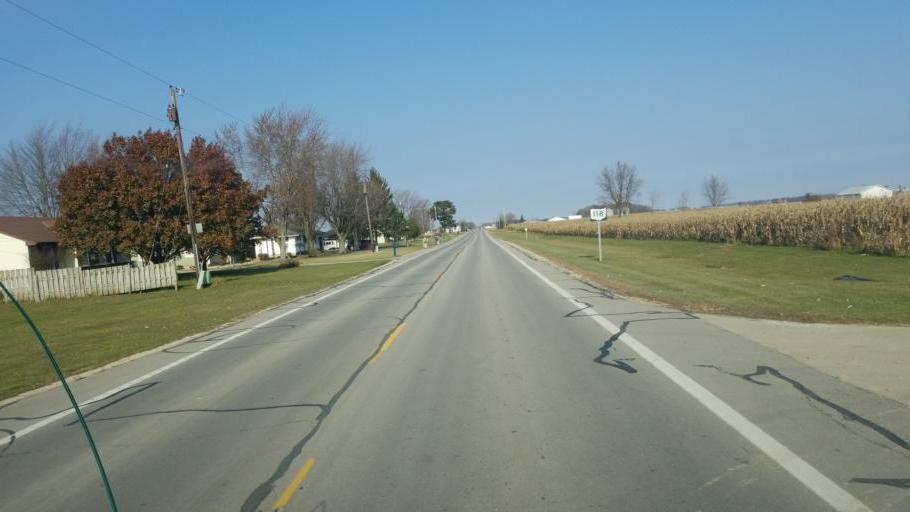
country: US
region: Ohio
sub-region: Mercer County
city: Coldwater
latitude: 40.5094
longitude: -84.6286
